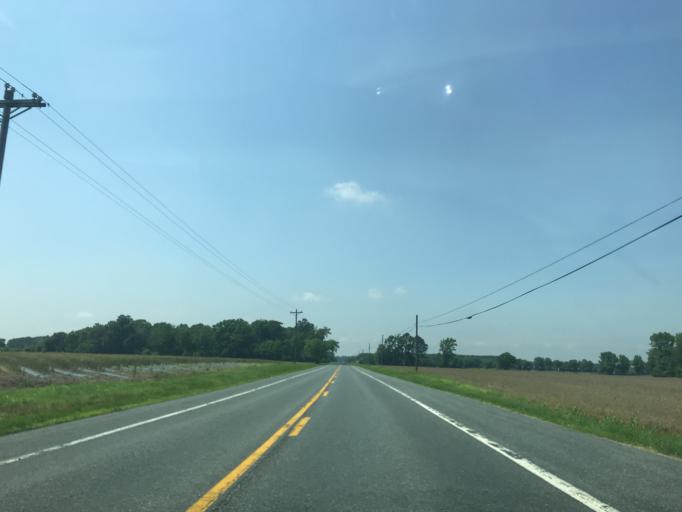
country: US
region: Maryland
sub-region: Caroline County
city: Federalsburg
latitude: 38.6456
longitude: -75.7143
